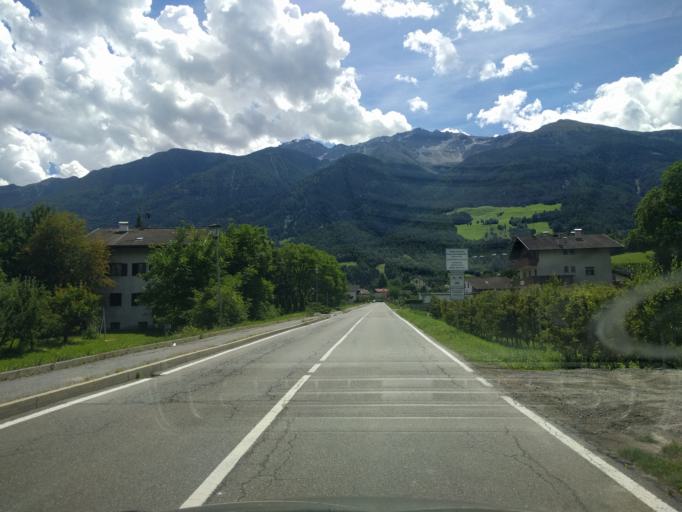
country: IT
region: Trentino-Alto Adige
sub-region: Bolzano
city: Prato Allo Stelvio
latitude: 46.6227
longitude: 10.5836
